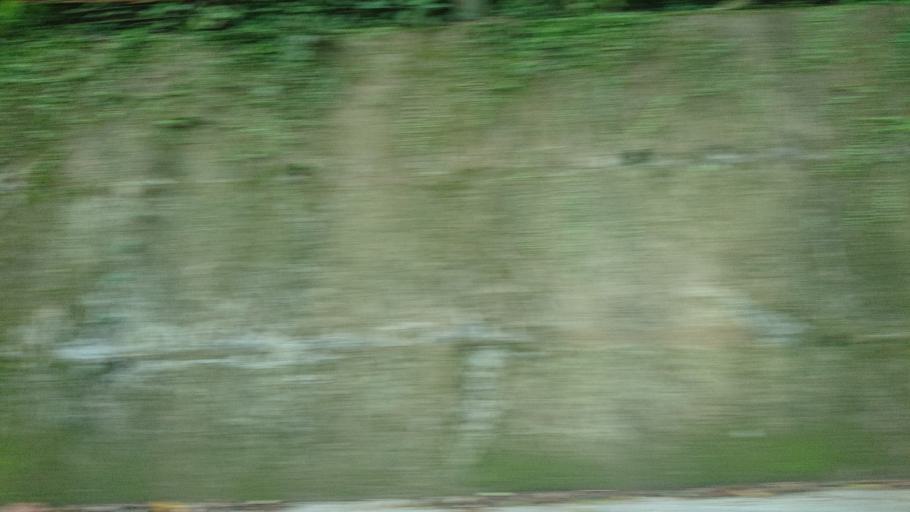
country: TW
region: Taiwan
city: Daxi
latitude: 24.8782
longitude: 121.3808
